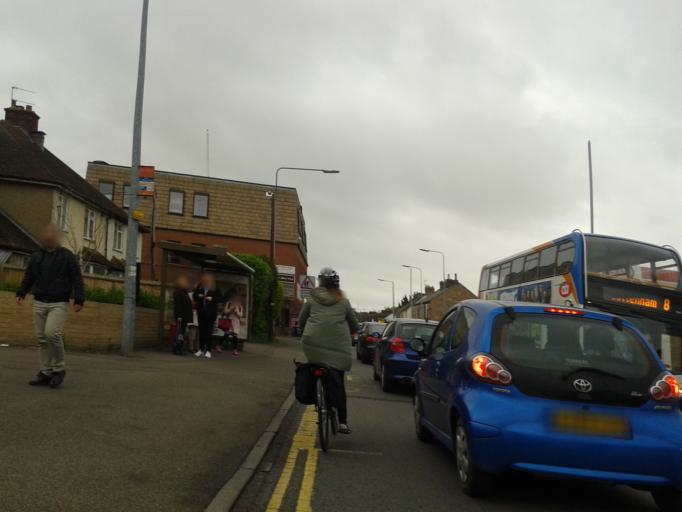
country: GB
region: England
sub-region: Cambridgeshire
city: Cambridge
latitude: 52.2198
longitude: 0.1117
